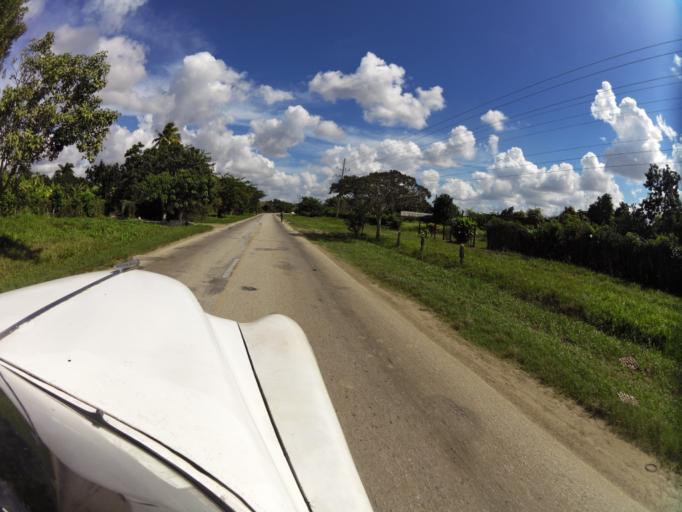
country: CU
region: Holguin
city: Cacocum
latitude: 20.8597
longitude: -76.4522
